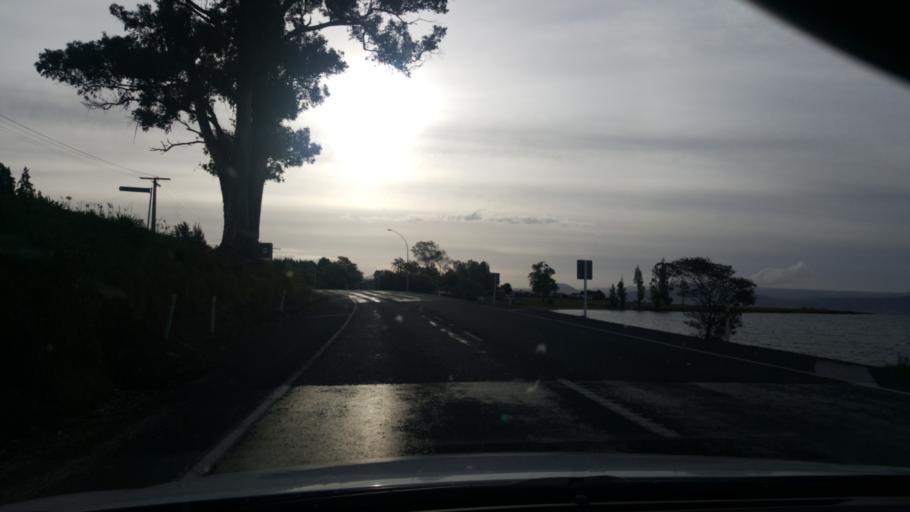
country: NZ
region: Waikato
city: Turangi
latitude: -38.9058
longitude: 175.9269
